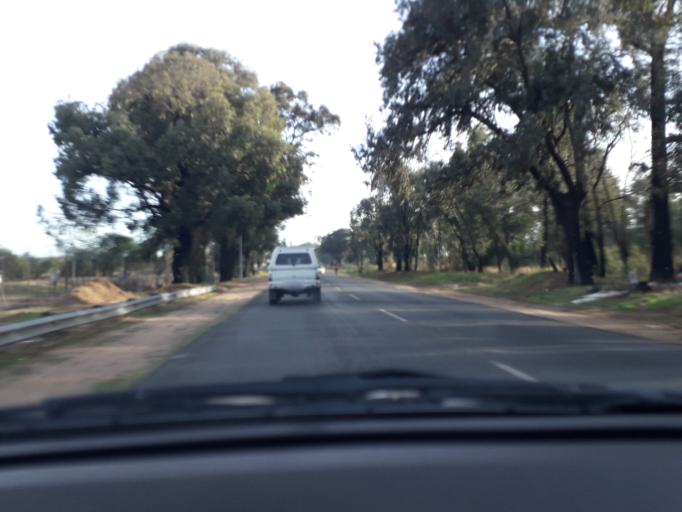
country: ZA
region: Gauteng
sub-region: City of Tshwane Metropolitan Municipality
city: Centurion
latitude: -25.9150
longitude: 28.1579
